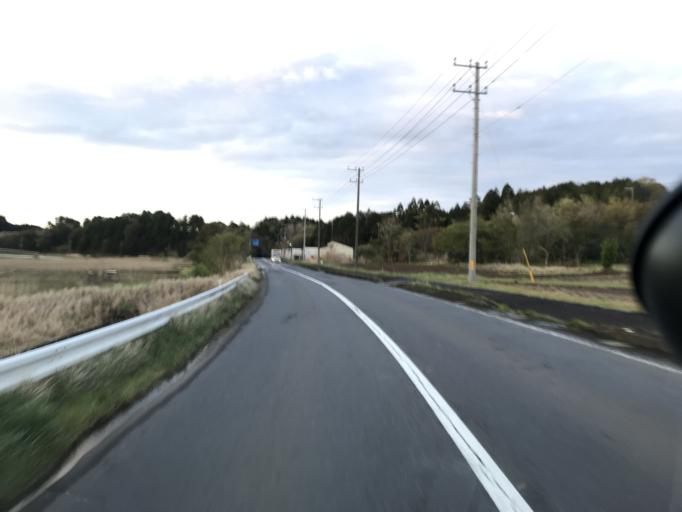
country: JP
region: Chiba
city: Sawara
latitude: 35.8139
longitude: 140.4934
